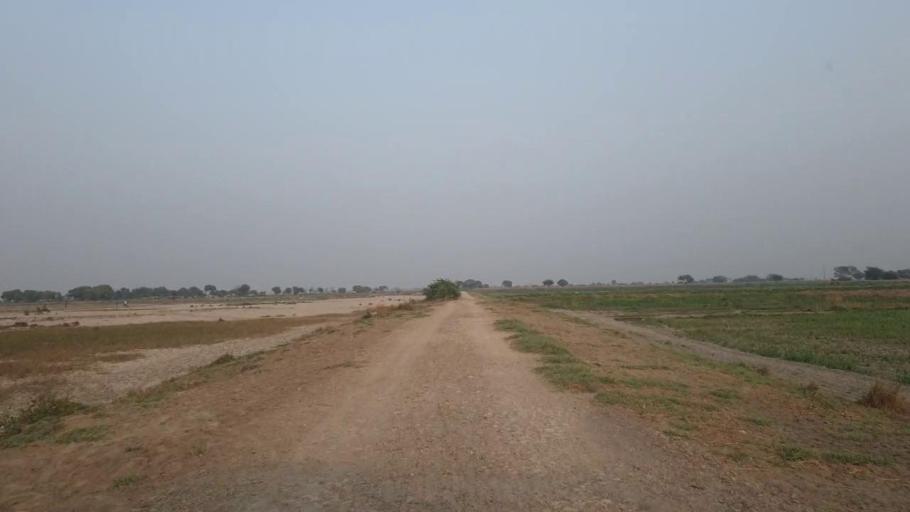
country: PK
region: Sindh
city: Mirpur Batoro
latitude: 24.6605
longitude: 68.3815
